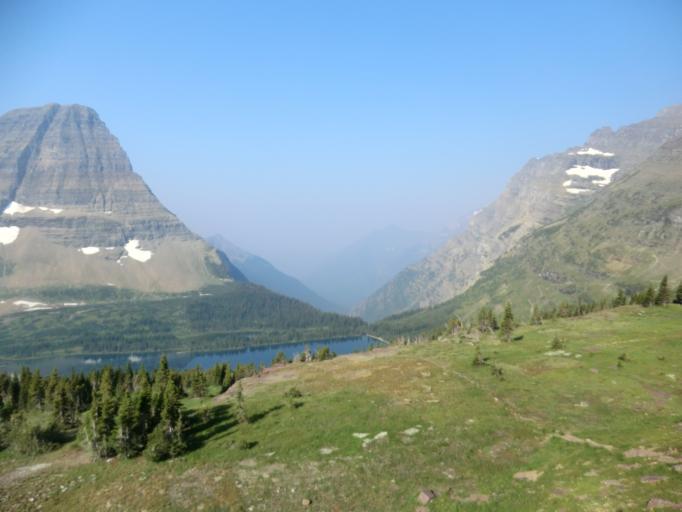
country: US
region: Montana
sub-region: Flathead County
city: Columbia Falls
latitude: 48.6873
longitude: -113.7417
